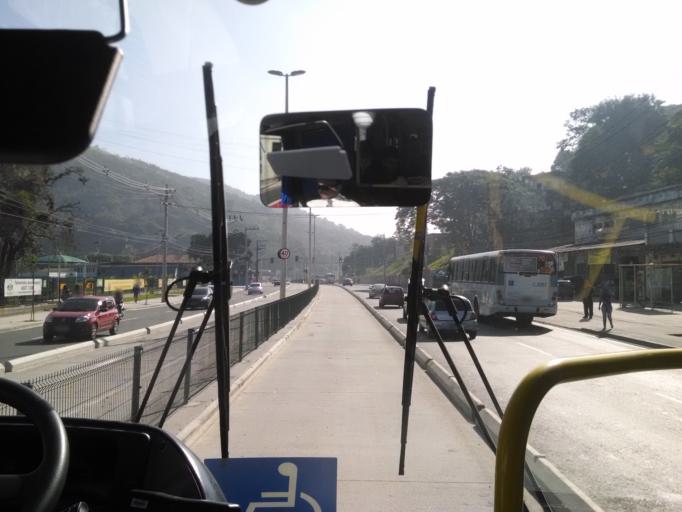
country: BR
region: Rio de Janeiro
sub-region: Sao Joao De Meriti
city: Sao Joao de Meriti
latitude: -22.9132
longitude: -43.3605
